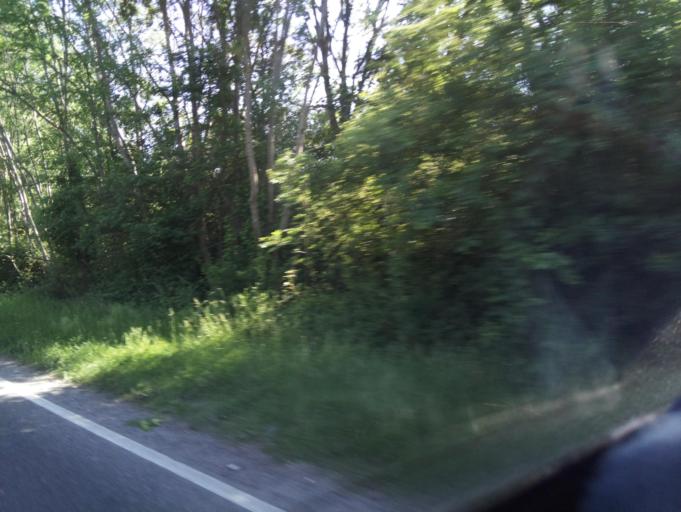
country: GB
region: England
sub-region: Hampshire
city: Andover
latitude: 51.2081
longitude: -1.4528
